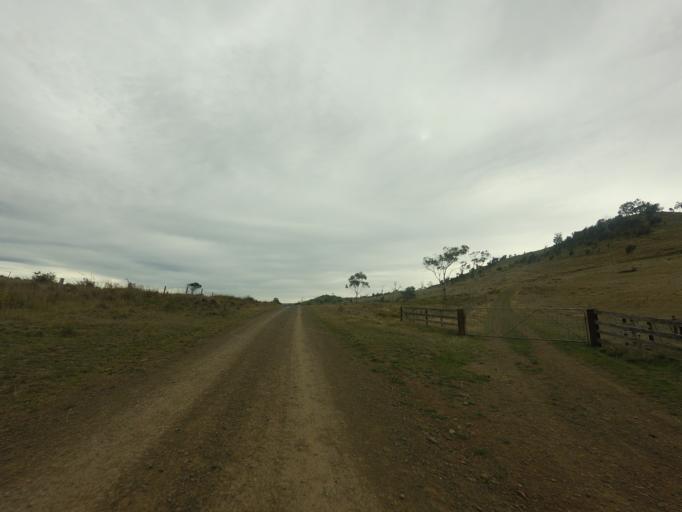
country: AU
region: Tasmania
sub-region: Derwent Valley
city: New Norfolk
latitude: -42.3731
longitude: 146.8613
